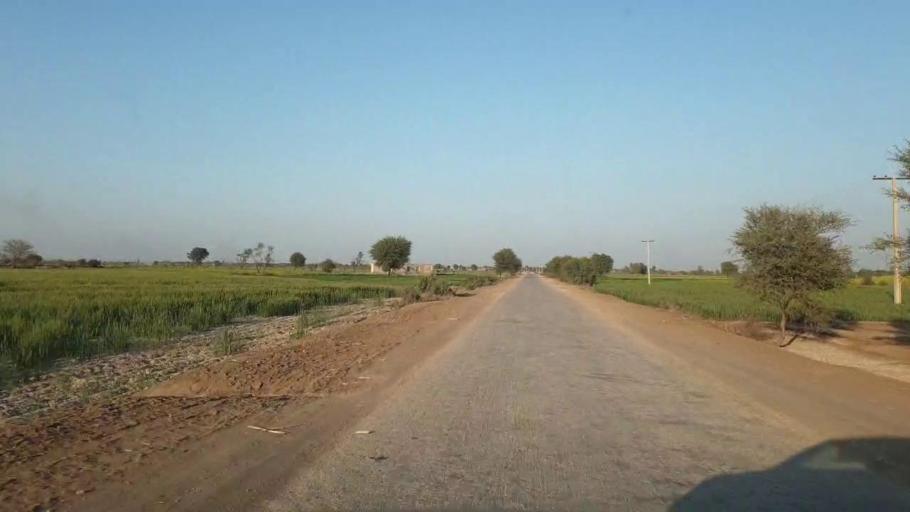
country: PK
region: Sindh
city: Tando Allahyar
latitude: 25.3781
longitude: 68.7488
